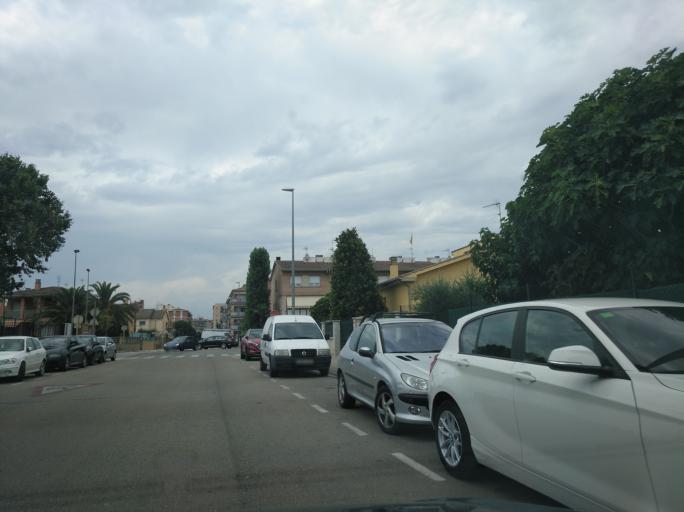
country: ES
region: Catalonia
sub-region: Provincia de Girona
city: Salt
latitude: 41.9686
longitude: 2.7914
